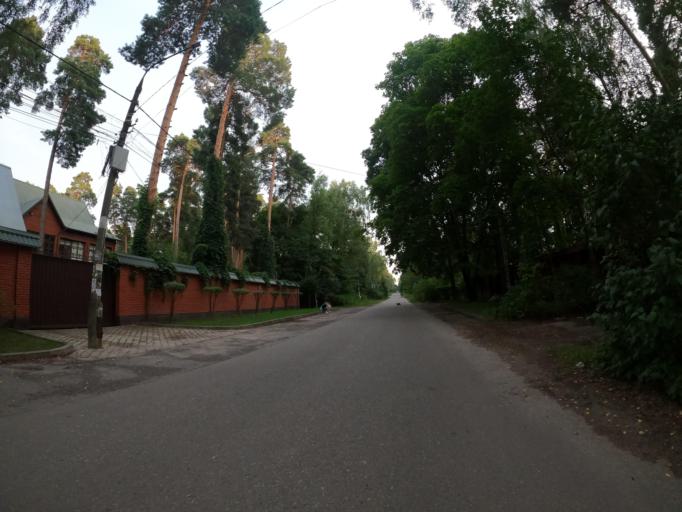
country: RU
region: Moskovskaya
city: Bykovo
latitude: 55.6374
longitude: 38.0796
